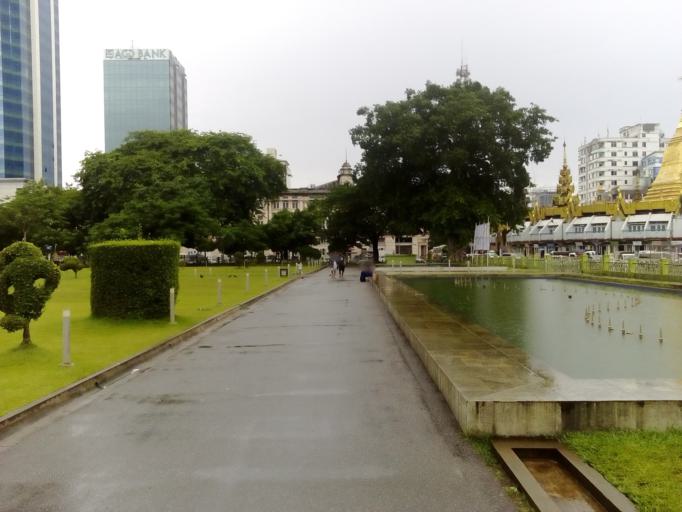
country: MM
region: Yangon
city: Yangon
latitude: 16.7737
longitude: 96.1600
